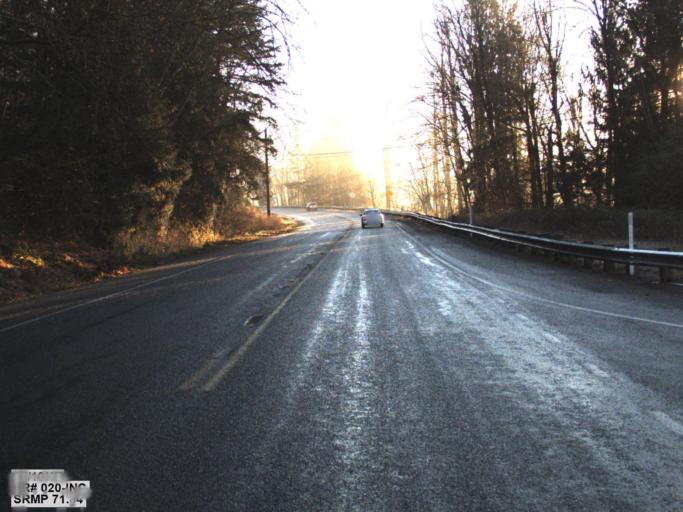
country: US
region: Washington
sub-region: Skagit County
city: Sedro-Woolley
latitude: 48.5260
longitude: -122.1203
